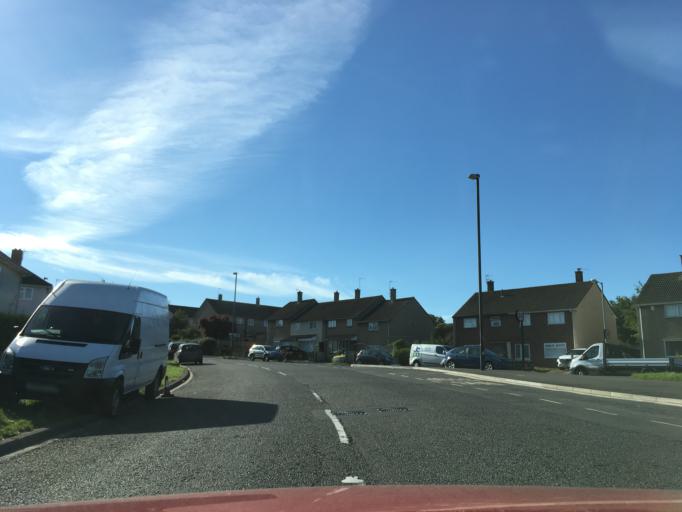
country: GB
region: England
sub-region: Bath and North East Somerset
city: Whitchurch
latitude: 51.4108
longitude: -2.5534
